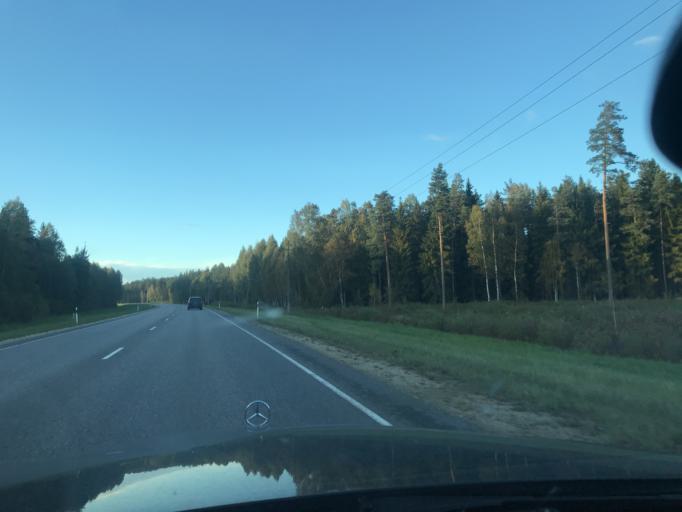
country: EE
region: Vorumaa
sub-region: Voru linn
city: Voru
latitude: 57.8330
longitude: 27.0614
